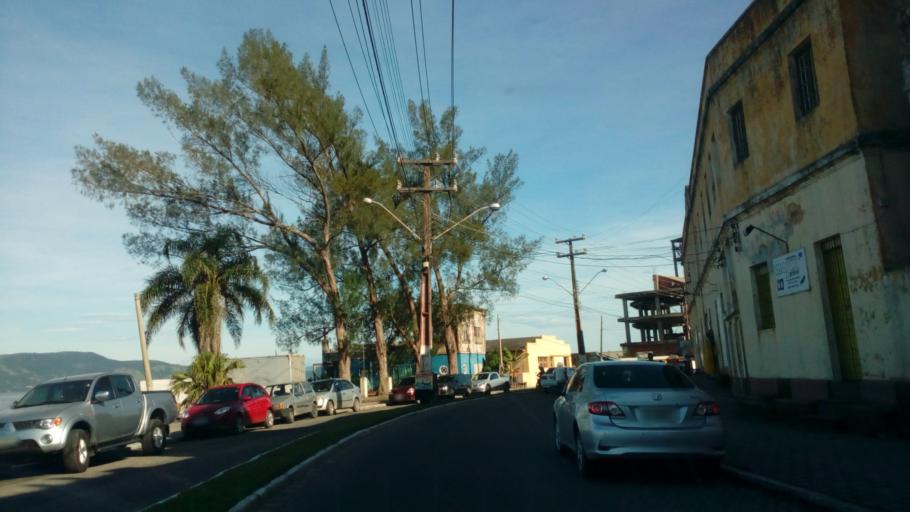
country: BR
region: Santa Catarina
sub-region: Laguna
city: Laguna
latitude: -28.4817
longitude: -48.7848
